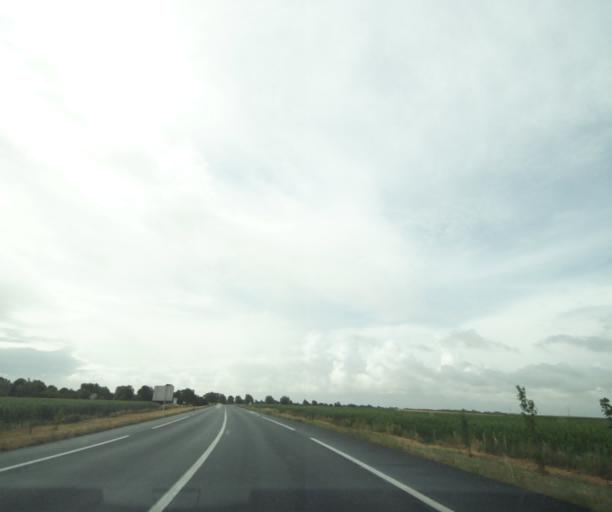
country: FR
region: Pays de la Loire
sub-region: Departement de la Vendee
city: Champagne-les-Marais
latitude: 46.3735
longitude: -1.0917
